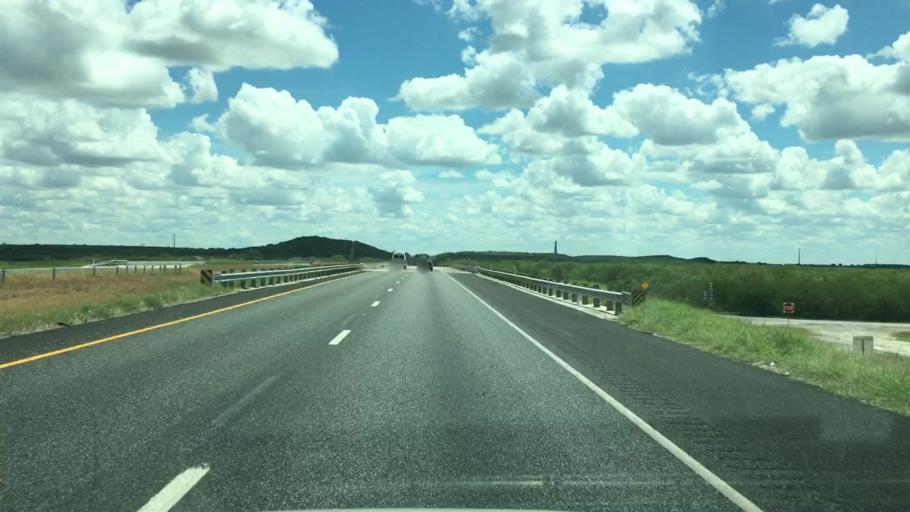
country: US
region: Texas
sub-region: Live Oak County
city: Three Rivers
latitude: 28.7347
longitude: -98.2898
